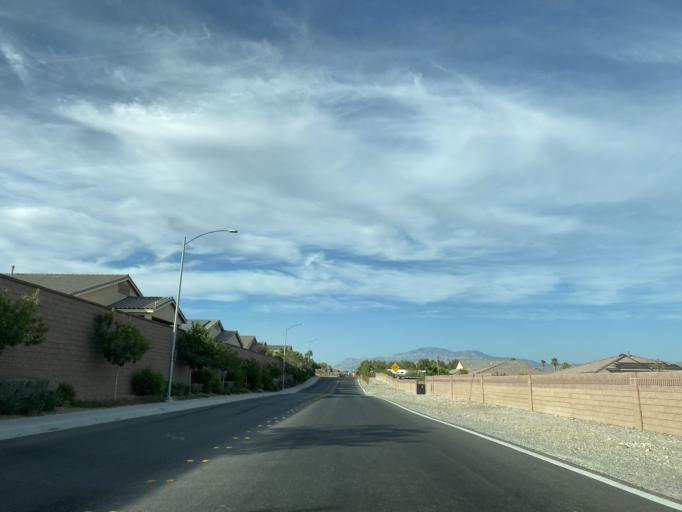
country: US
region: Nevada
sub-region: Clark County
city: Summerlin South
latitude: 36.2866
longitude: -115.3126
